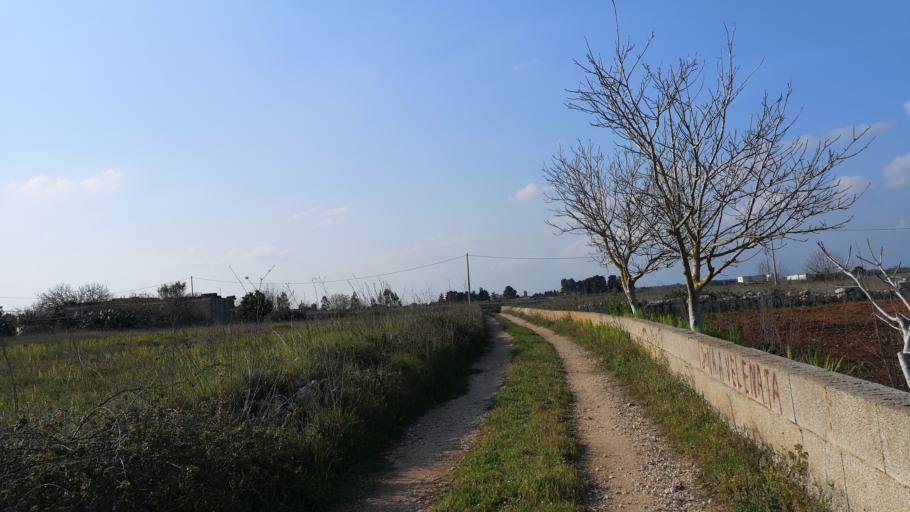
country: IT
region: Apulia
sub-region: Provincia di Lecce
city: Spongano
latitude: 40.0333
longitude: 18.3629
